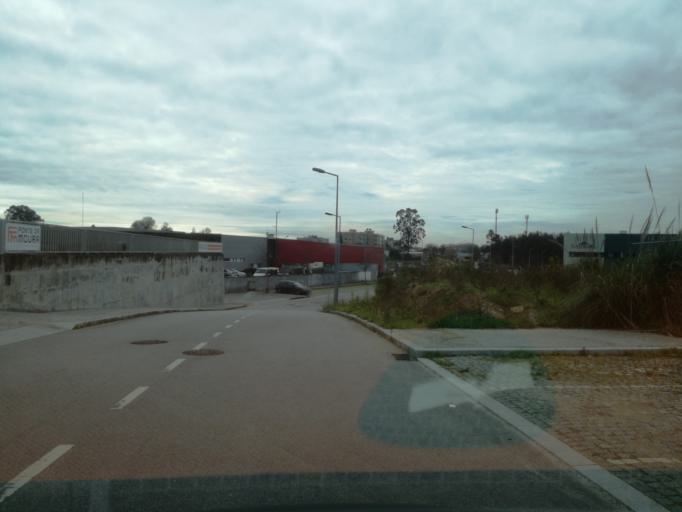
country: PT
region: Porto
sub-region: Maia
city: Anta
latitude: 41.2731
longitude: -8.6109
